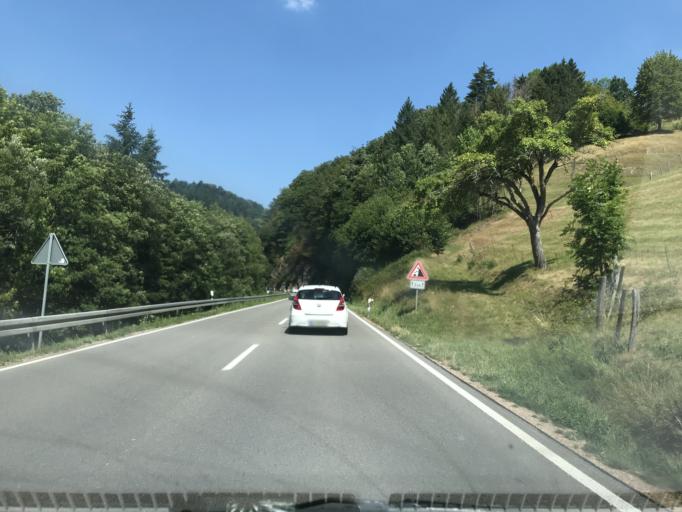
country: DE
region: Baden-Wuerttemberg
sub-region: Freiburg Region
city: Wembach
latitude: 47.7429
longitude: 7.8818
